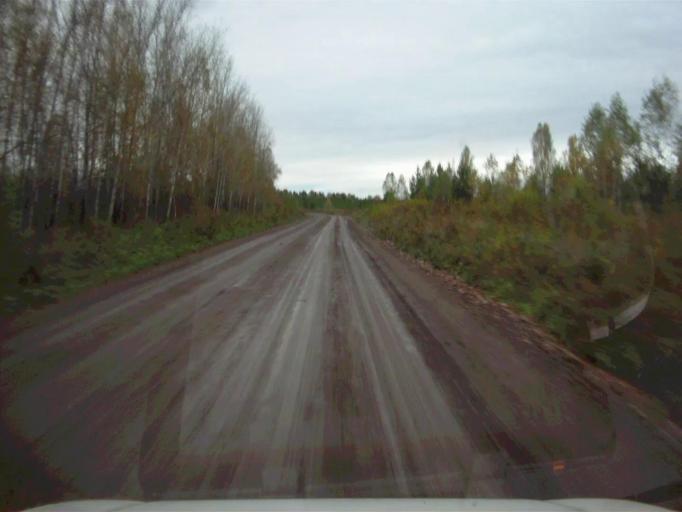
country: RU
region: Chelyabinsk
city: Nyazepetrovsk
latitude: 56.1380
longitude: 59.2997
